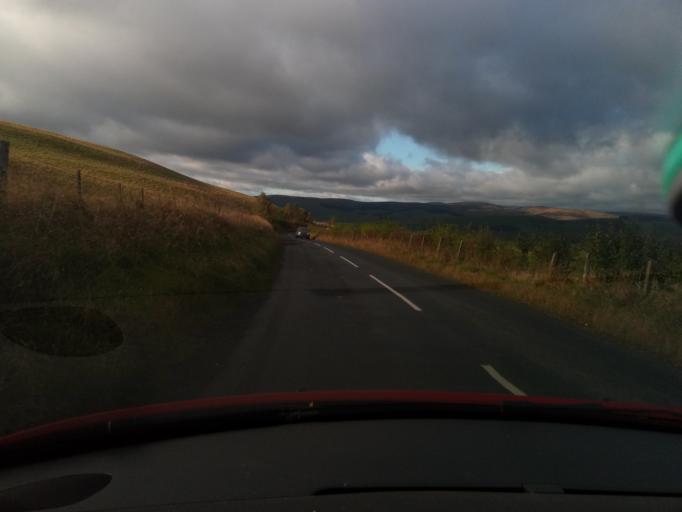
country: GB
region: Scotland
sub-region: The Scottish Borders
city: Lauder
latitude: 55.7007
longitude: -2.8310
